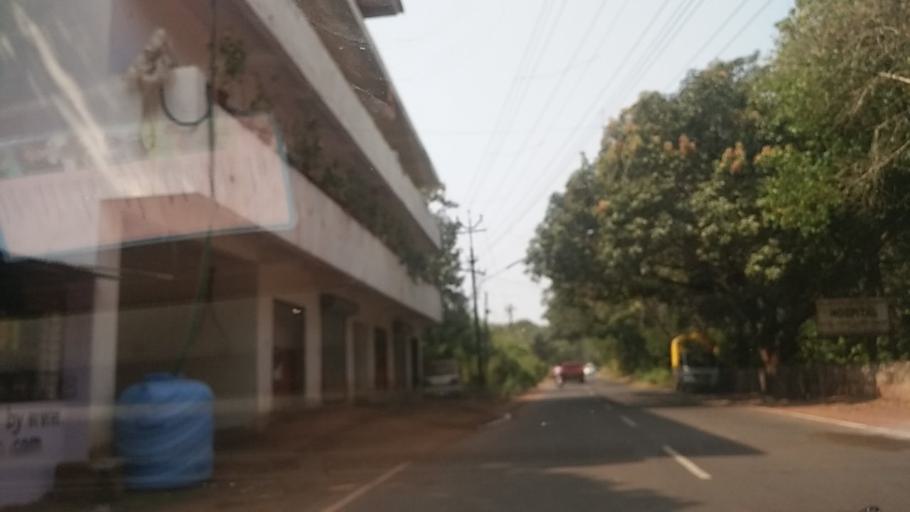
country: IN
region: Goa
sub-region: North Goa
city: Morjim
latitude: 15.6575
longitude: 73.7463
